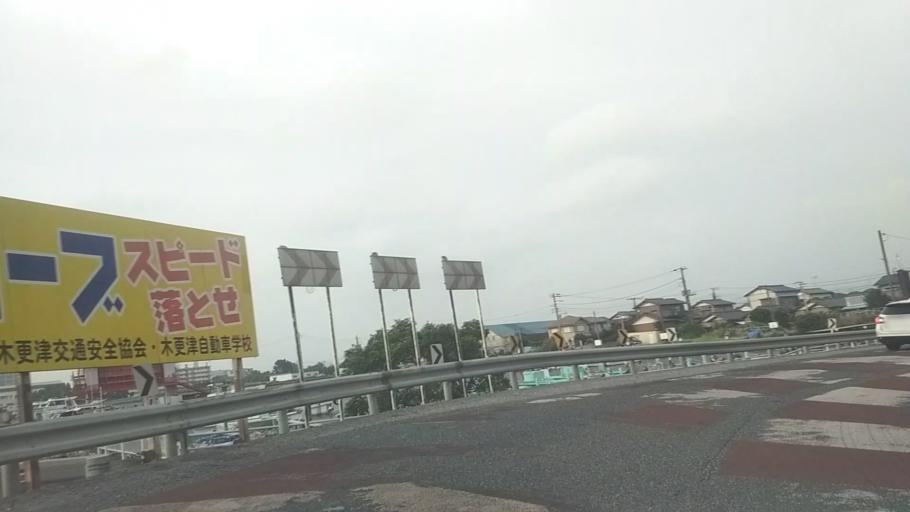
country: JP
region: Chiba
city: Kisarazu
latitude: 35.3853
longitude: 139.9181
